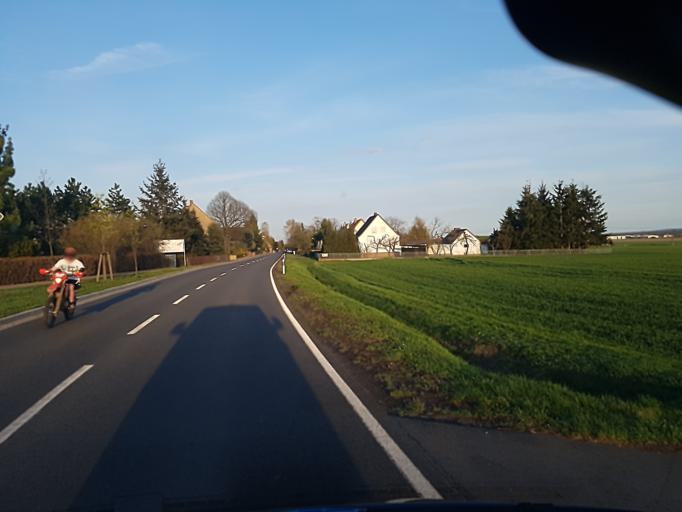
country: DE
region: Saxony
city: Zinna
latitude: 51.5676
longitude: 12.9487
